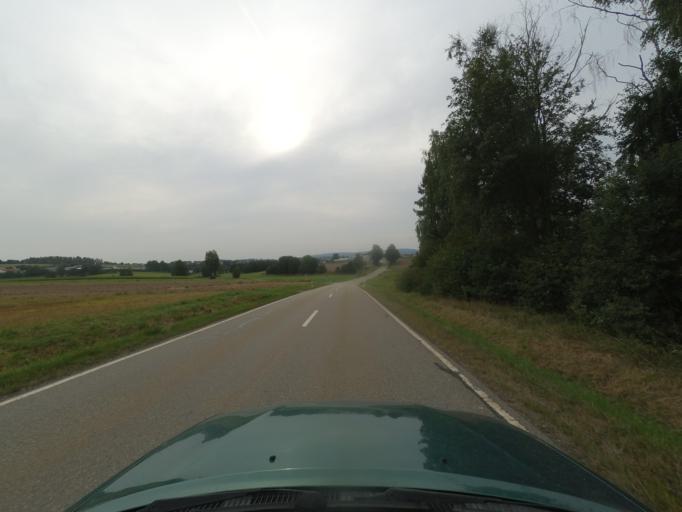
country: DE
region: Bavaria
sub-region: Upper Palatinate
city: Eslarn
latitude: 49.5859
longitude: 12.5014
